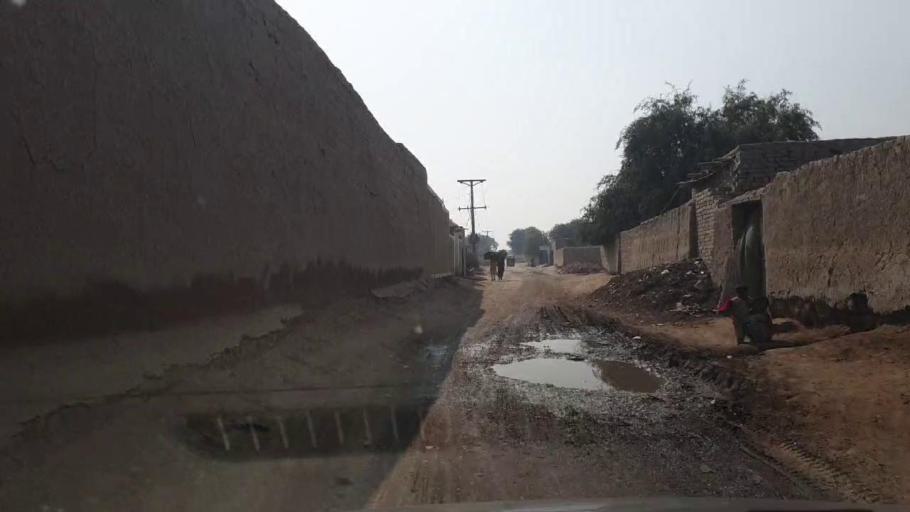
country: PK
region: Sindh
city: Hala
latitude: 25.8924
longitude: 68.4409
